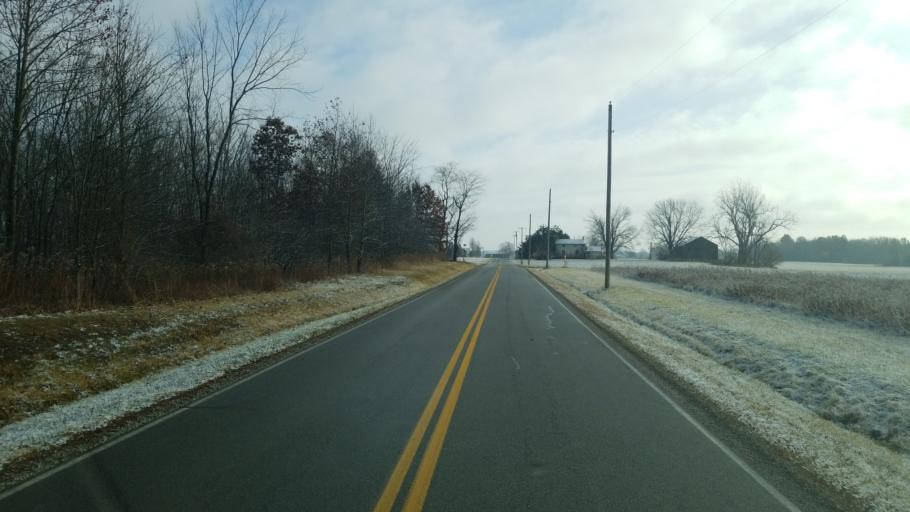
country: US
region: Ohio
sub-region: Crawford County
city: Crestline
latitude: 40.8087
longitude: -82.7468
